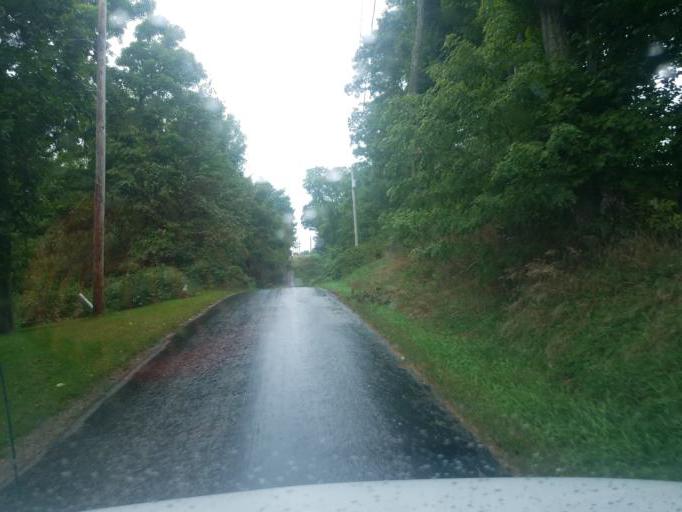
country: US
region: Ohio
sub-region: Wayne County
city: West Salem
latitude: 40.9300
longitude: -82.1296
